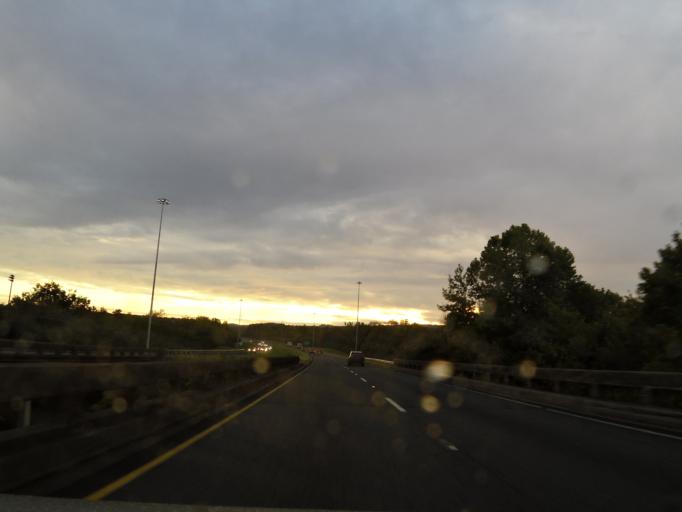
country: US
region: Alabama
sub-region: Jefferson County
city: Clay
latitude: 33.6598
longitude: -86.5896
